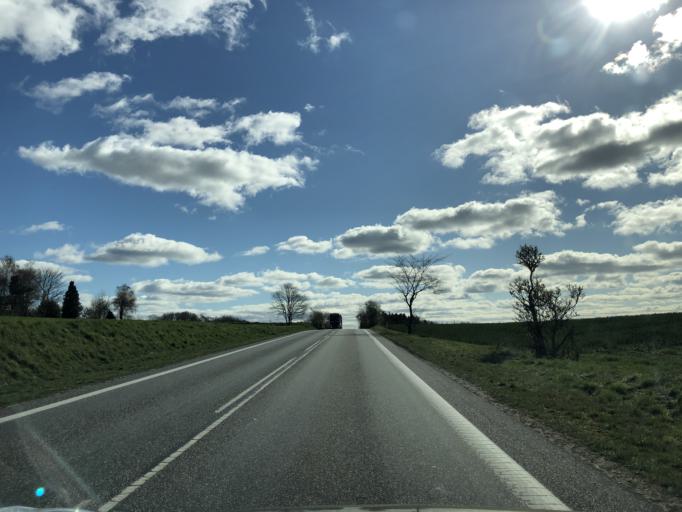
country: DK
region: North Denmark
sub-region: Mariagerfjord Kommune
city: Hobro
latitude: 56.6140
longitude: 9.6344
